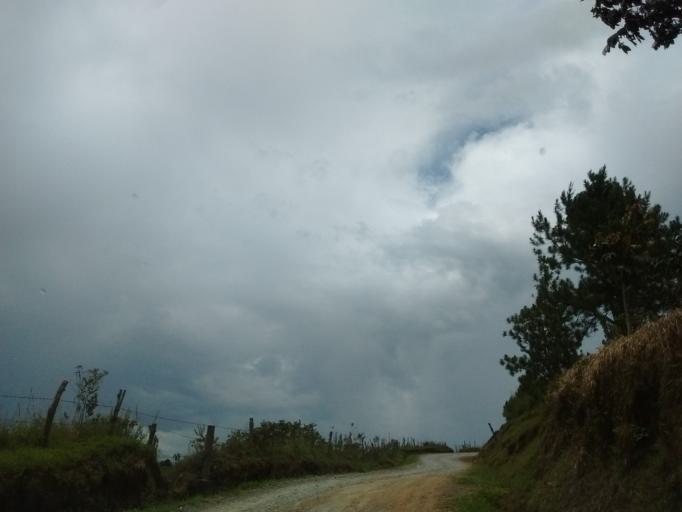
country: CO
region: Cauca
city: Cajibio
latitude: 2.5547
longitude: -76.6346
